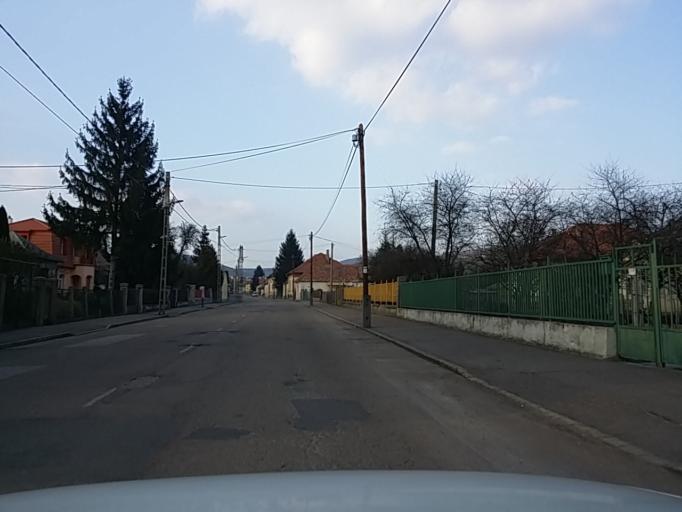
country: HU
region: Borsod-Abauj-Zemplen
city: Putnok
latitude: 48.2897
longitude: 20.4370
